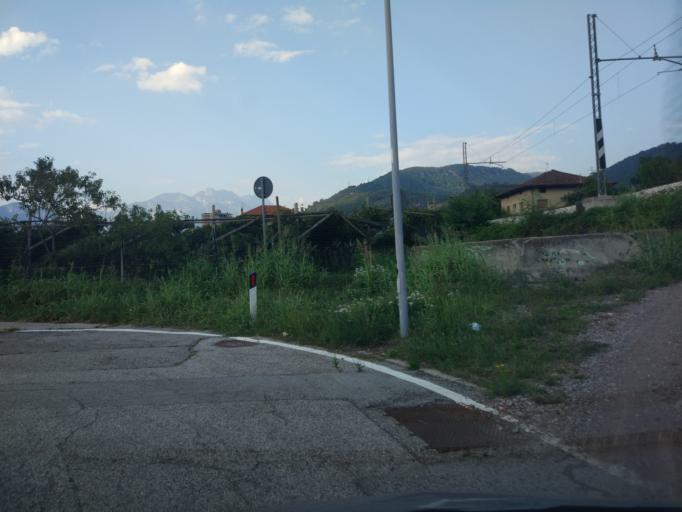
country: IT
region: Trentino-Alto Adige
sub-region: Provincia di Trento
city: Lavis
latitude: 46.1326
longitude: 11.1099
